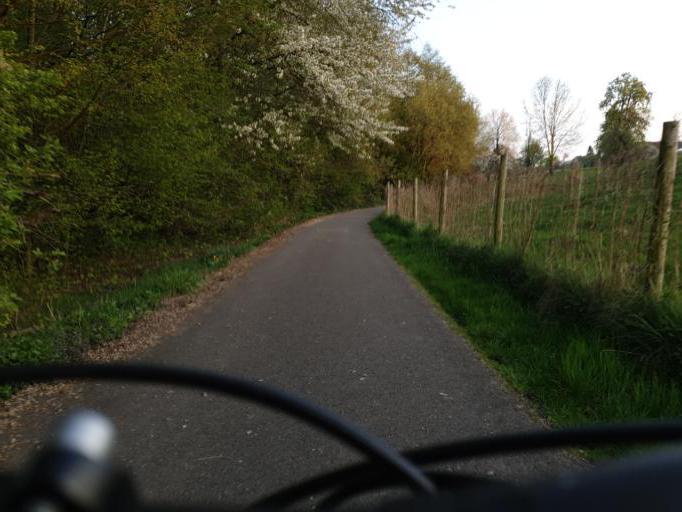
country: DE
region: North Rhine-Westphalia
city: Opladen
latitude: 51.0624
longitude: 7.0627
